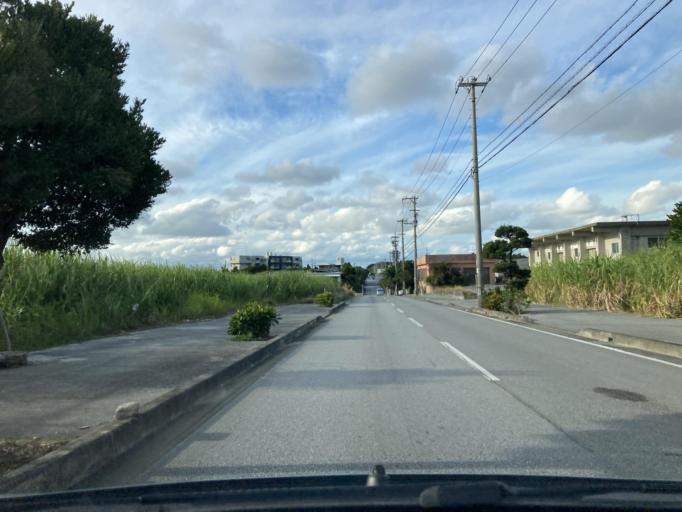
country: JP
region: Okinawa
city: Itoman
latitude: 26.1390
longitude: 127.7369
